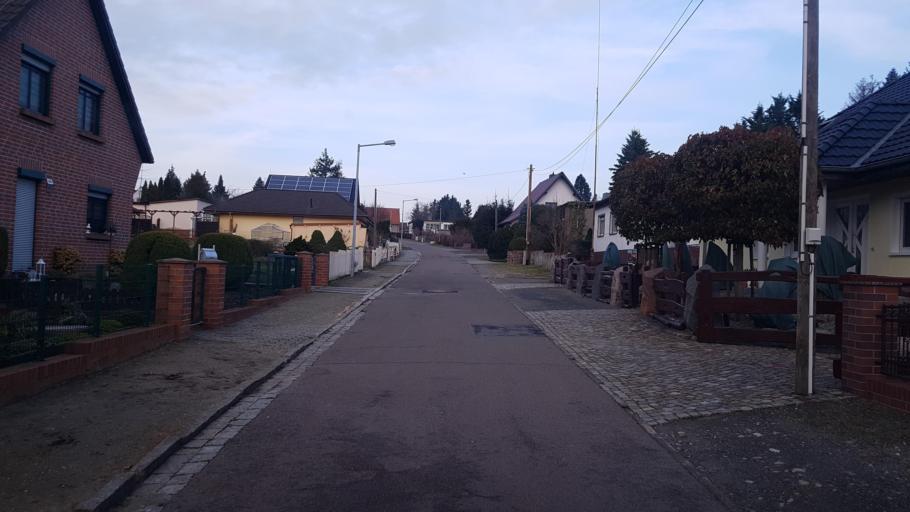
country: DE
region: Brandenburg
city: Lauchhammer
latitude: 51.4978
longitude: 13.7600
